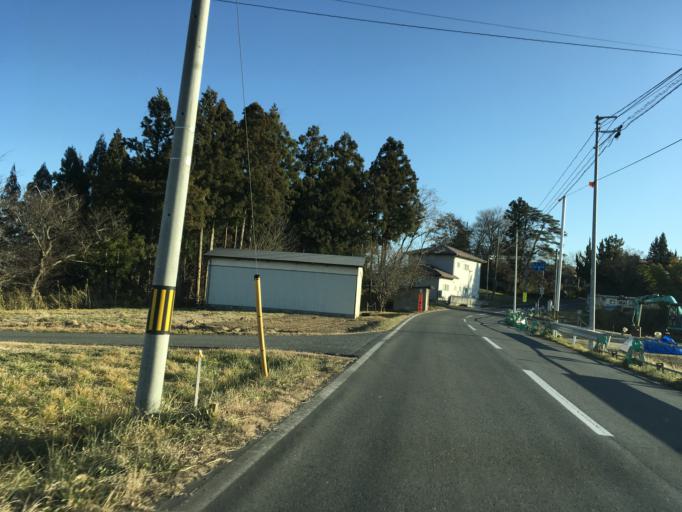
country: JP
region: Iwate
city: Ichinoseki
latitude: 38.7828
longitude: 141.2231
